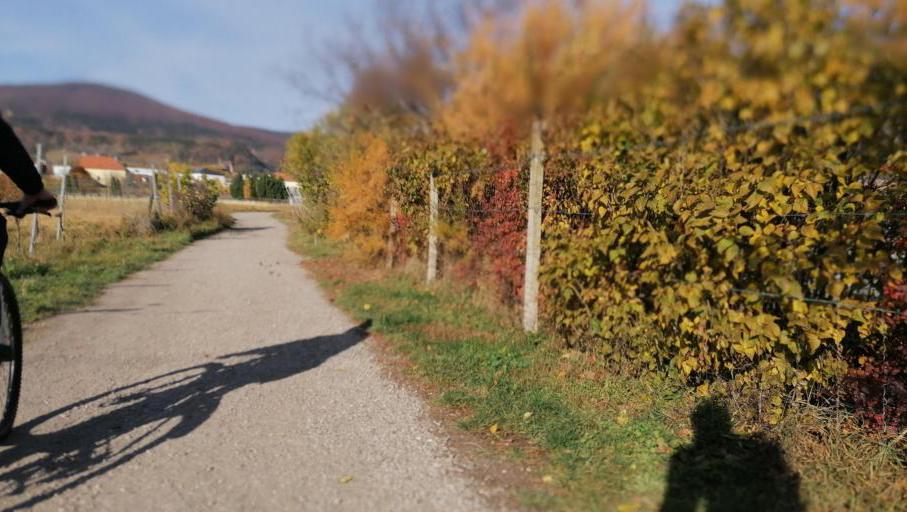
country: AT
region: Lower Austria
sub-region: Politischer Bezirk Modling
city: Gumpoldskirchen
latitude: 48.0429
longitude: 16.2870
